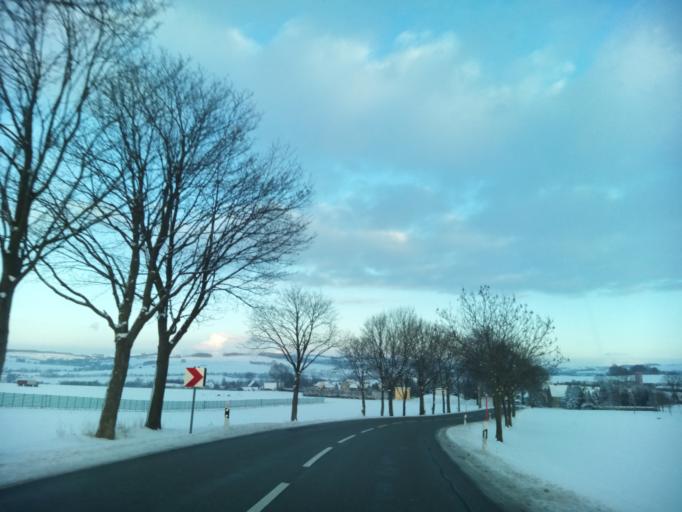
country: DE
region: Saxony
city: Eppendorf
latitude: 50.7827
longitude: 13.2200
